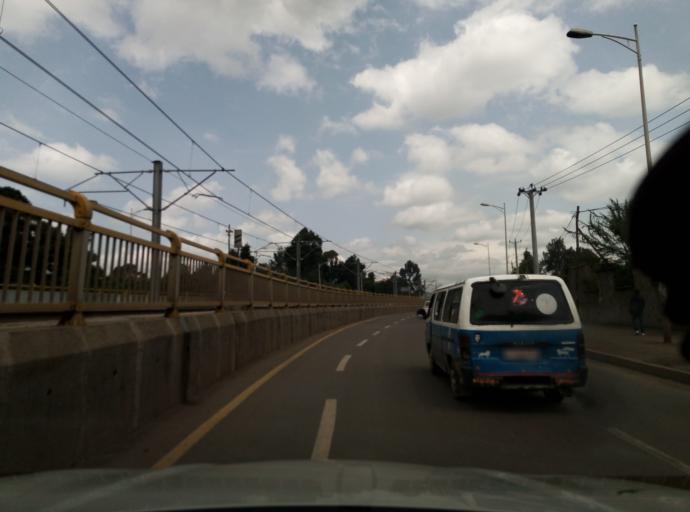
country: ET
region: Adis Abeba
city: Addis Ababa
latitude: 9.0107
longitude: 38.7247
